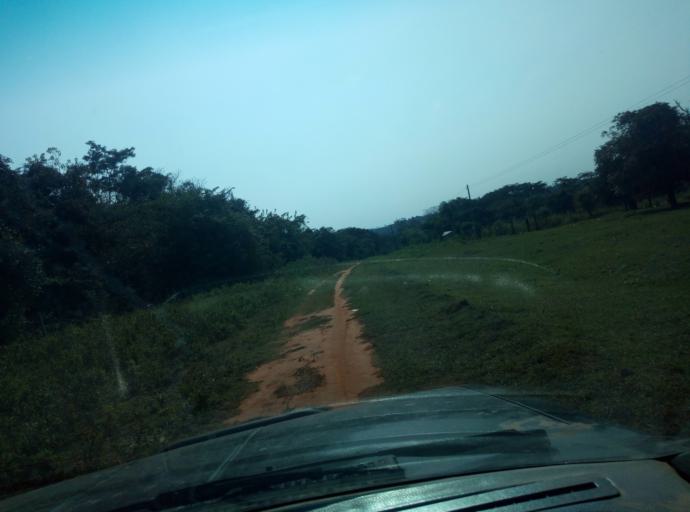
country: PY
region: Caaguazu
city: Carayao
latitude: -25.3042
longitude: -56.3242
